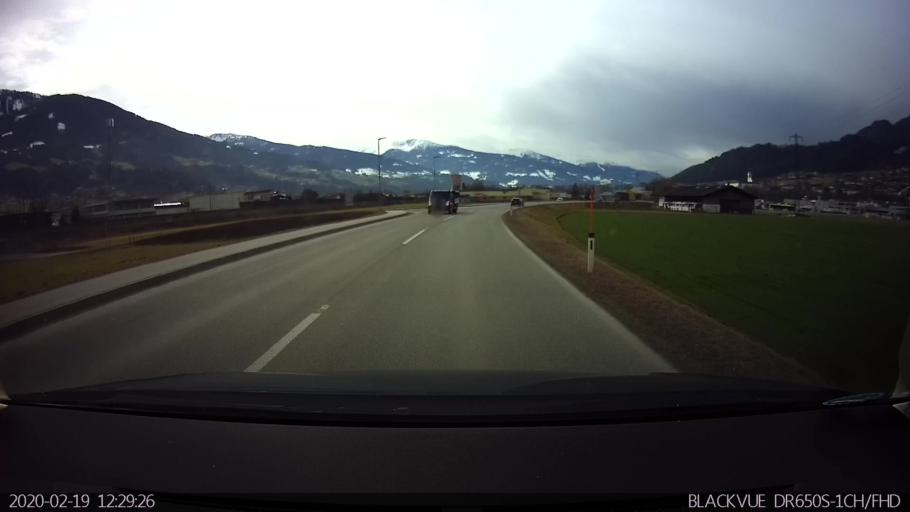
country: AT
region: Tyrol
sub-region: Politischer Bezirk Schwaz
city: Schwaz
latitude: 47.3602
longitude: 11.7103
